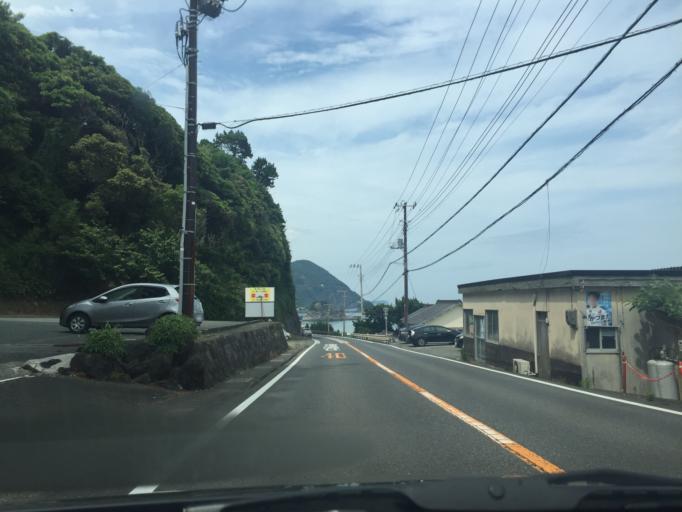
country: JP
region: Shizuoka
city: Shimoda
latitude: 34.6995
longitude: 138.9743
